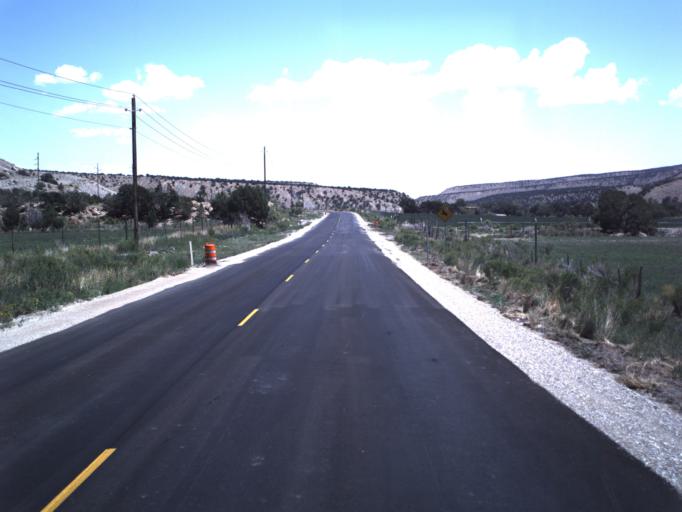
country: US
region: Utah
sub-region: Emery County
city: Orangeville
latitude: 39.2757
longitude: -111.1707
